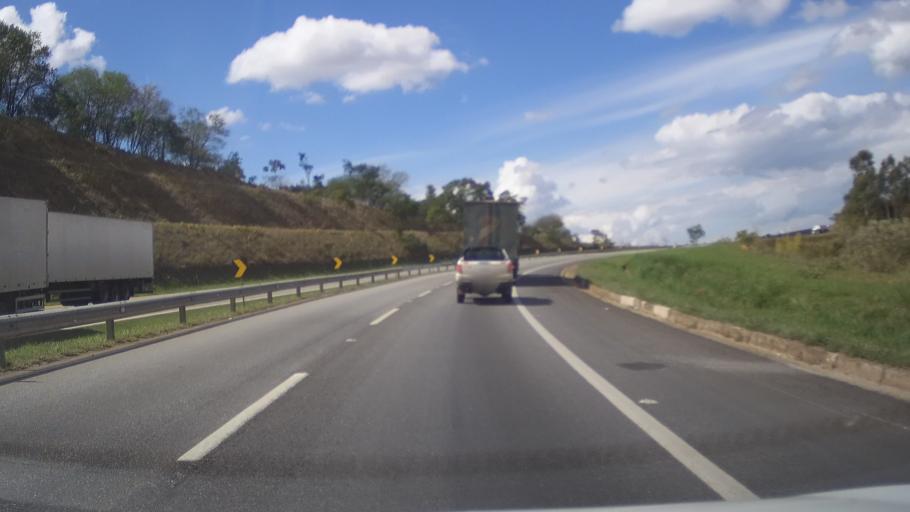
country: BR
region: Minas Gerais
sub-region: Oliveira
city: Oliveira
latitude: -20.8331
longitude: -44.8248
